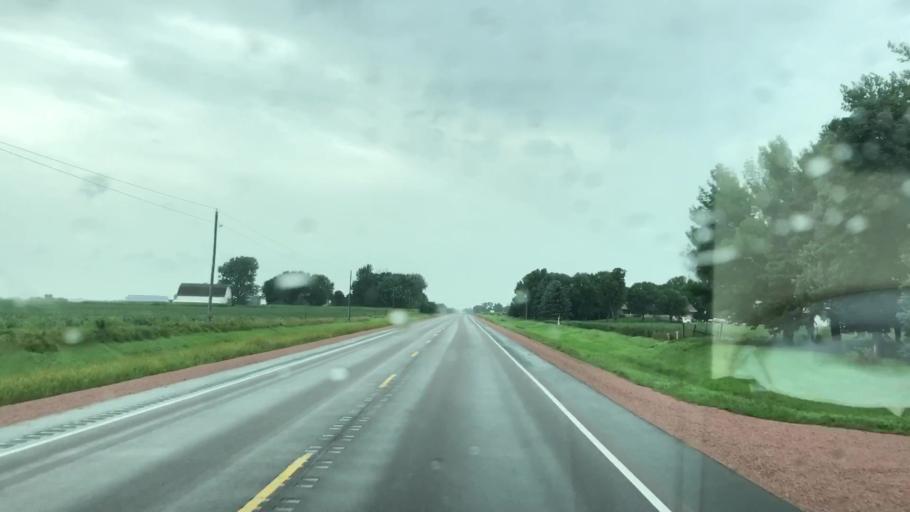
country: US
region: Iowa
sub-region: O'Brien County
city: Sanborn
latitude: 43.1862
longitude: -95.7452
